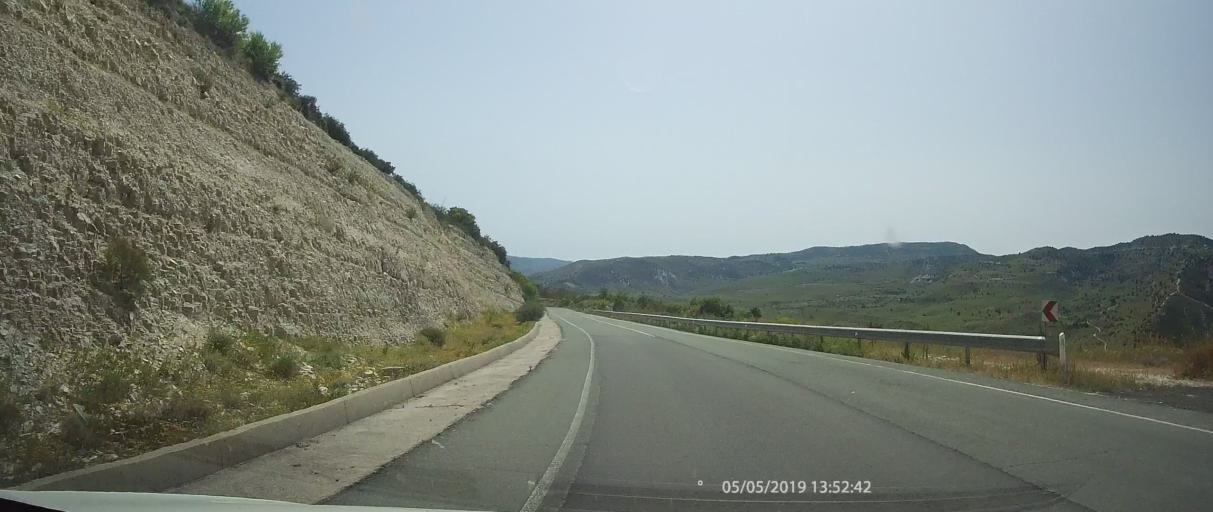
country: CY
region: Limassol
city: Pachna
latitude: 34.8284
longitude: 32.7296
